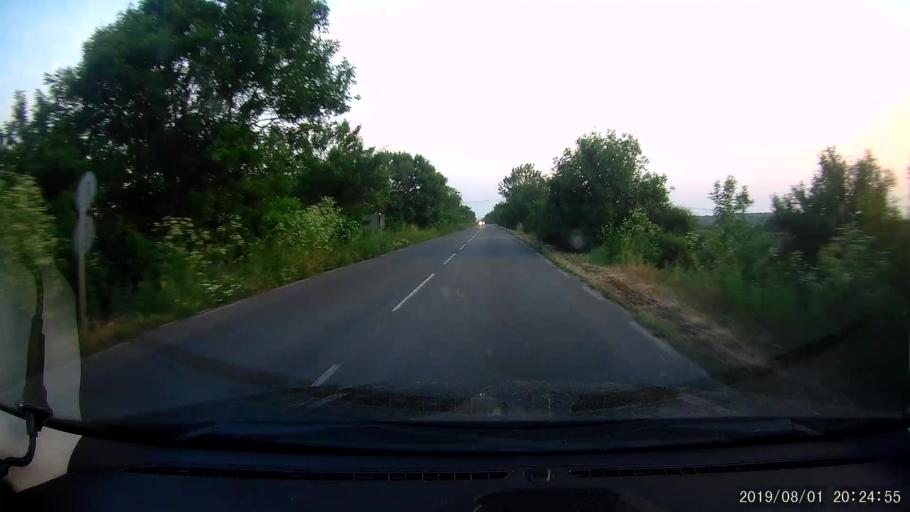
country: BG
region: Yambol
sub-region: Obshtina Elkhovo
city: Elkhovo
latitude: 42.2241
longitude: 26.5906
